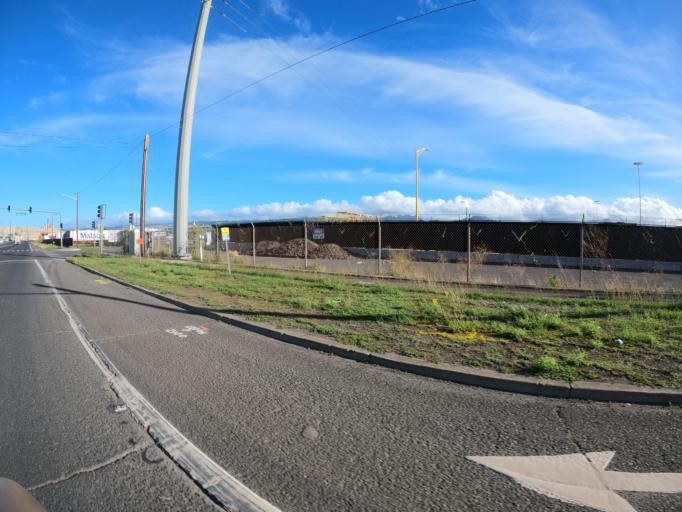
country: US
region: Hawaii
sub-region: Honolulu County
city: Honolulu
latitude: 21.3192
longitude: -157.8904
